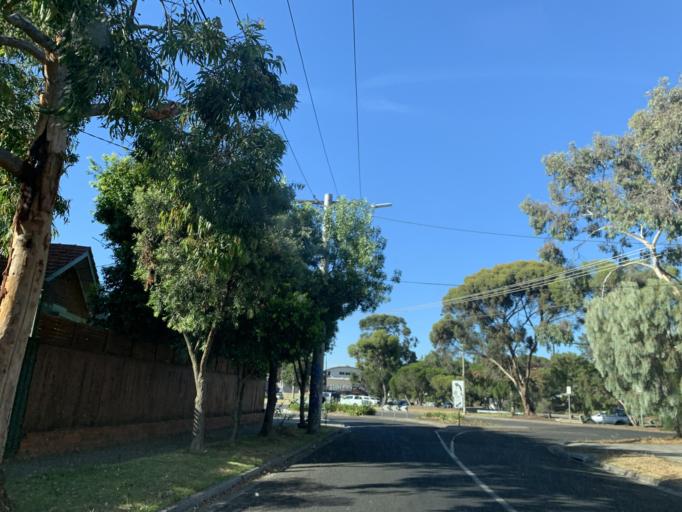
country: AU
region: Victoria
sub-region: Glen Eira
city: Elsternwick
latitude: -37.8955
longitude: 145.0052
